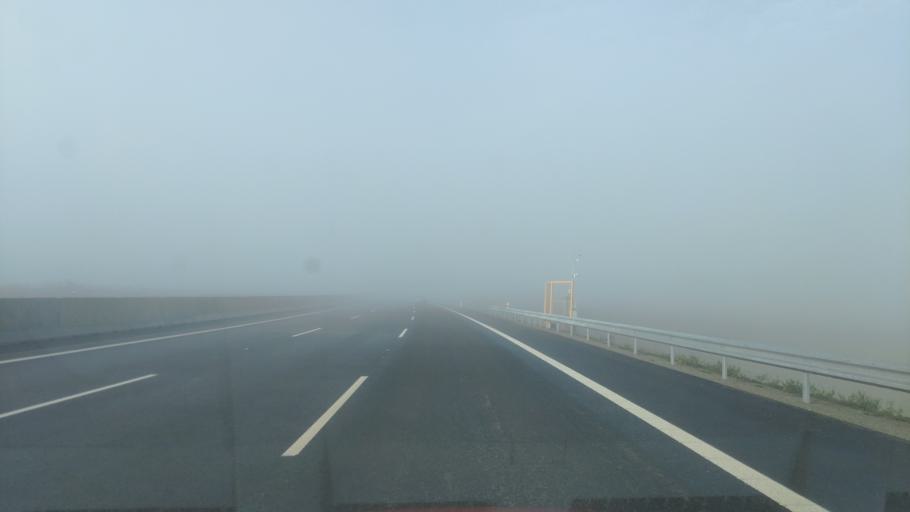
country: SK
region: Kosicky
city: Kosice
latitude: 48.7317
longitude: 21.4023
